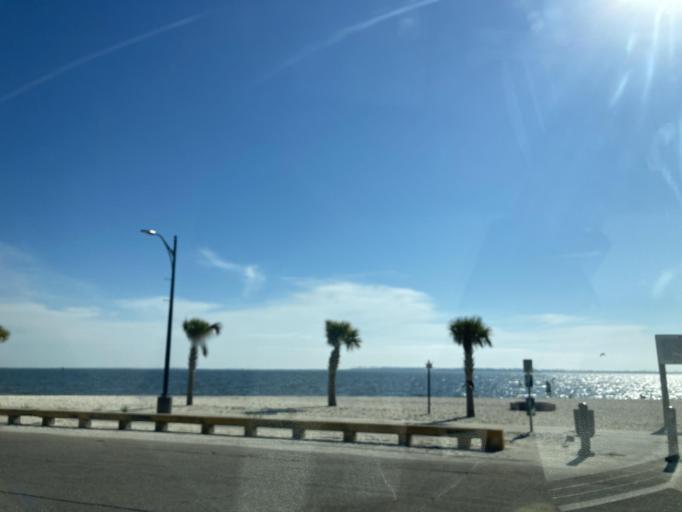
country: US
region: Mississippi
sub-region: Jackson County
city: Ocean Springs
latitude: 30.4046
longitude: -88.8278
